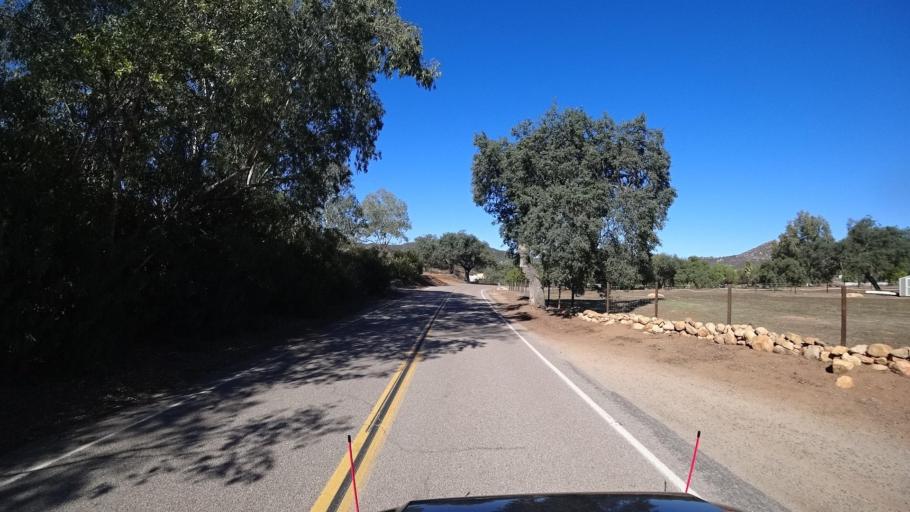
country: US
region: California
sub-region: San Diego County
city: Jamul
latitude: 32.7169
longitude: -116.8027
